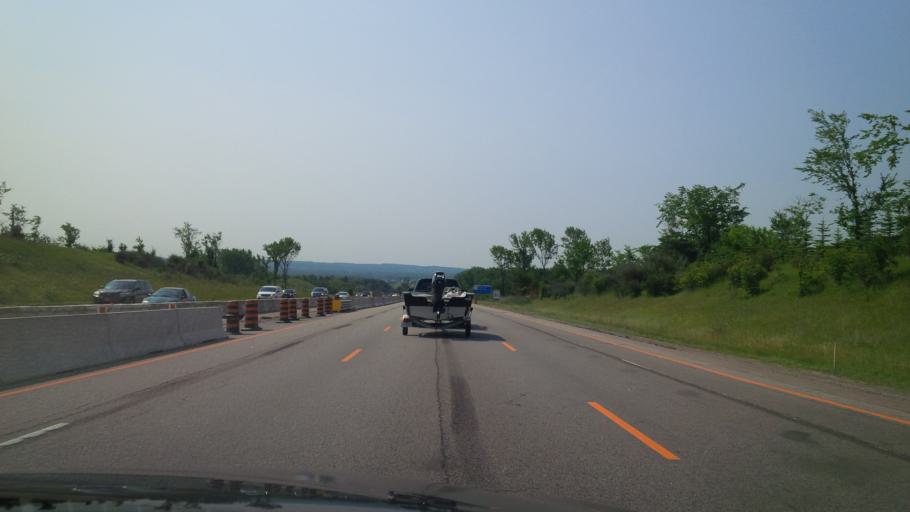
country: CA
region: Ontario
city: Innisfil
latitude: 44.2310
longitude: -79.6653
